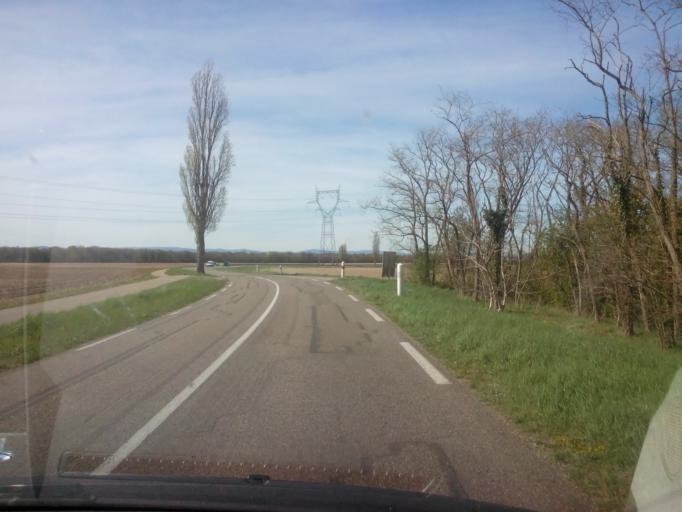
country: FR
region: Alsace
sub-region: Departement du Haut-Rhin
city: Fessenheim
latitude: 47.9455
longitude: 7.5409
